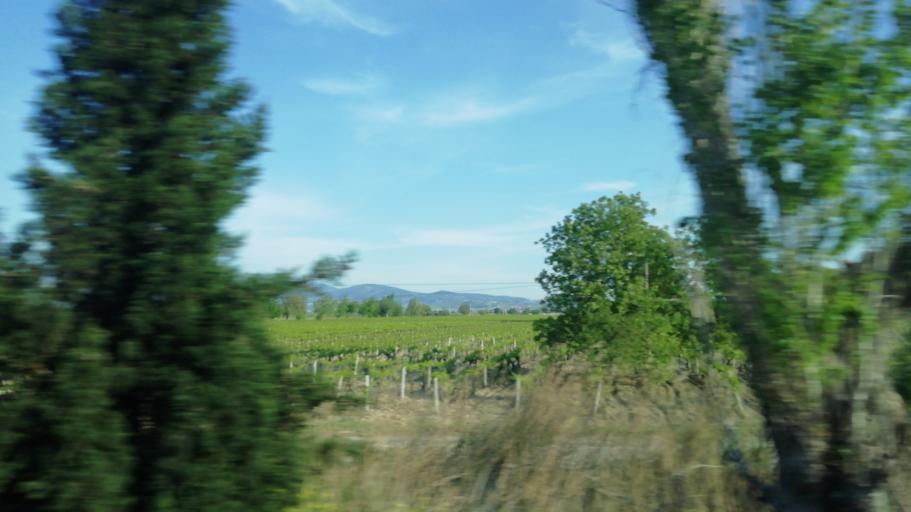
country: TR
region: Manisa
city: Saruhanli
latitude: 38.7448
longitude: 27.6112
